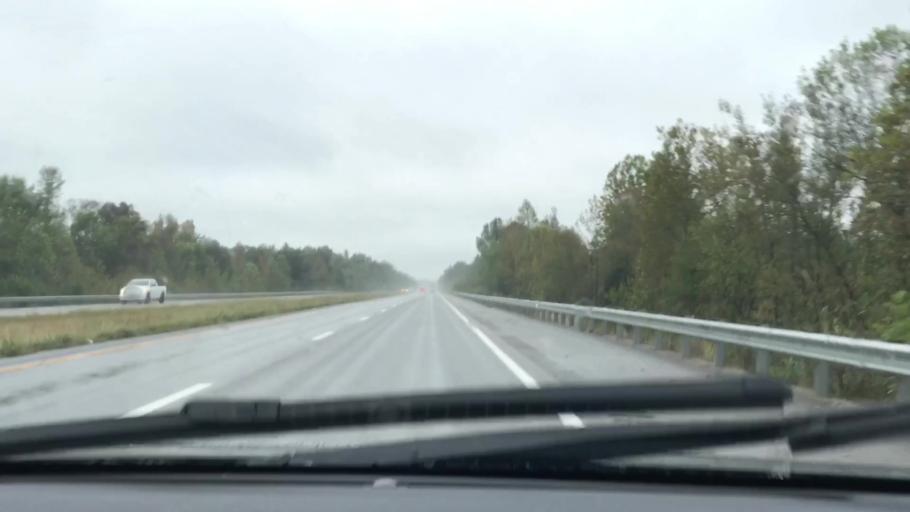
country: US
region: Kentucky
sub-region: Hopkins County
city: Nortonville
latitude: 37.1705
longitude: -87.4512
